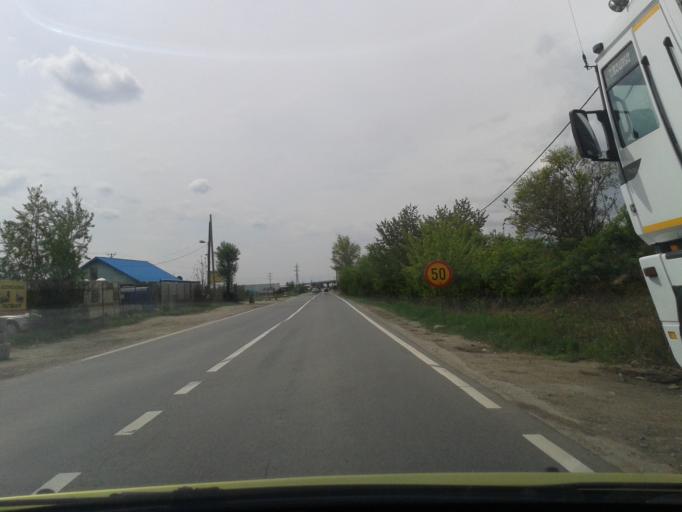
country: RO
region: Alba
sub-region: Municipiul Alba Iulia
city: Alba Iulia
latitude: 46.0562
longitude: 23.5787
